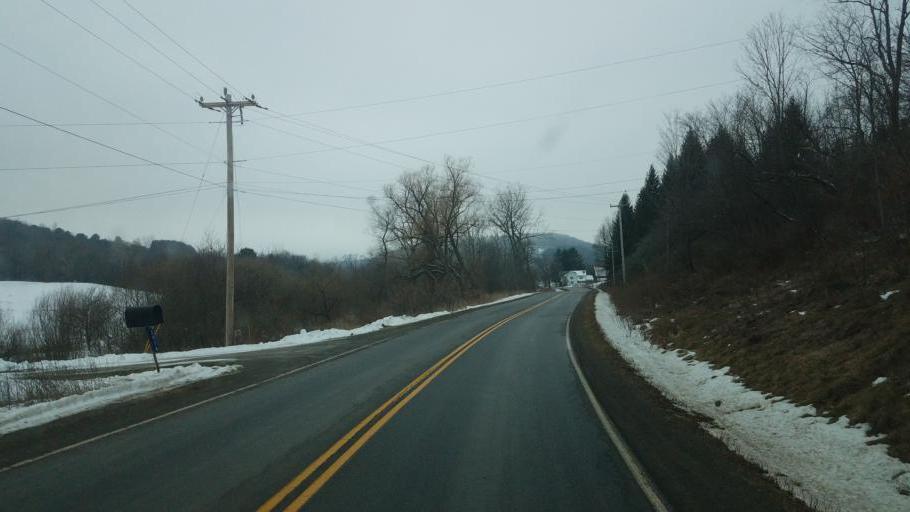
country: US
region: Pennsylvania
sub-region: Tioga County
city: Westfield
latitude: 42.0215
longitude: -77.5610
